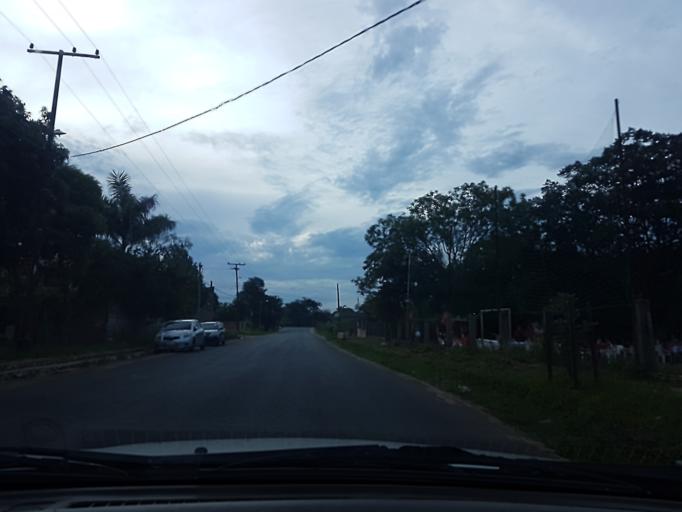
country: PY
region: Central
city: San Lorenzo
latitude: -25.2642
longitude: -57.4774
